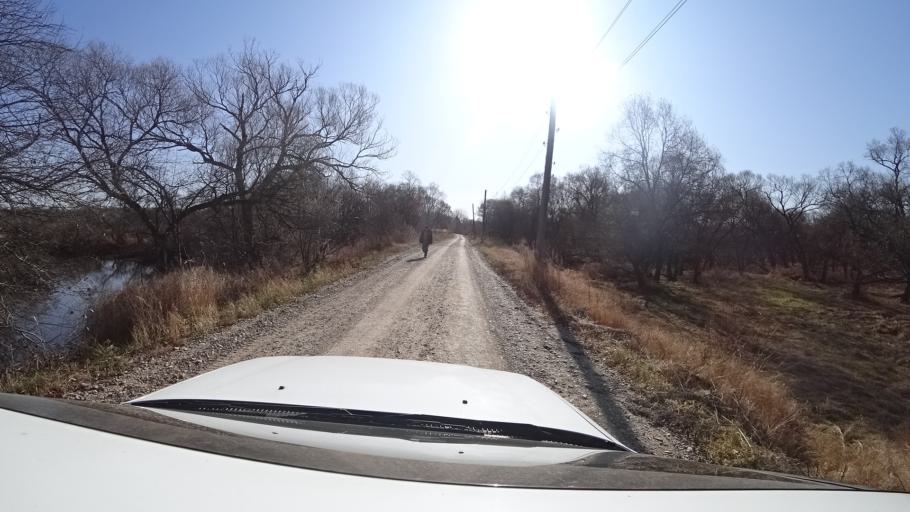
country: RU
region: Primorskiy
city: Lazo
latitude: 45.8819
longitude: 133.6412
